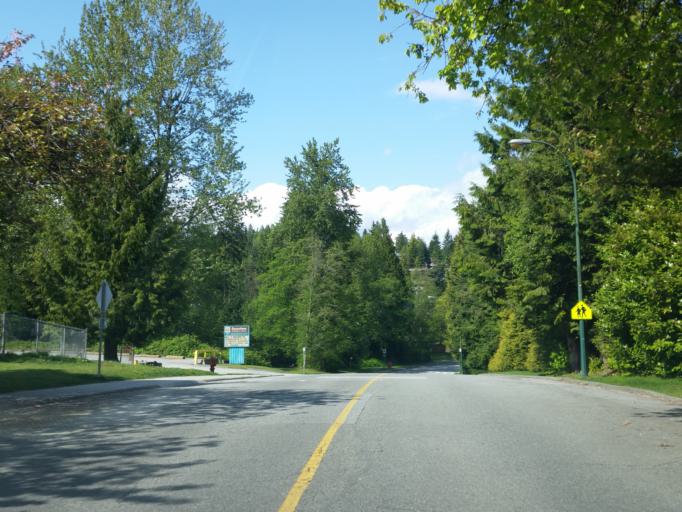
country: CA
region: British Columbia
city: Port Moody
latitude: 49.2794
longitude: -122.8755
